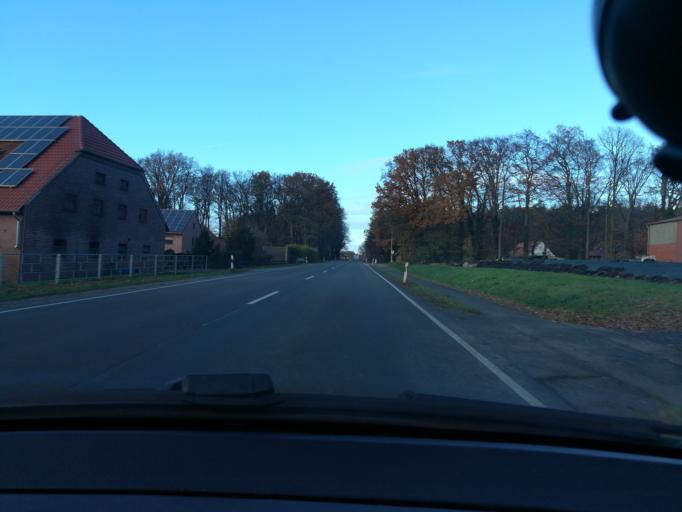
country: DE
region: Lower Saxony
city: Kirchdorf
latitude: 52.5695
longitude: 8.8488
